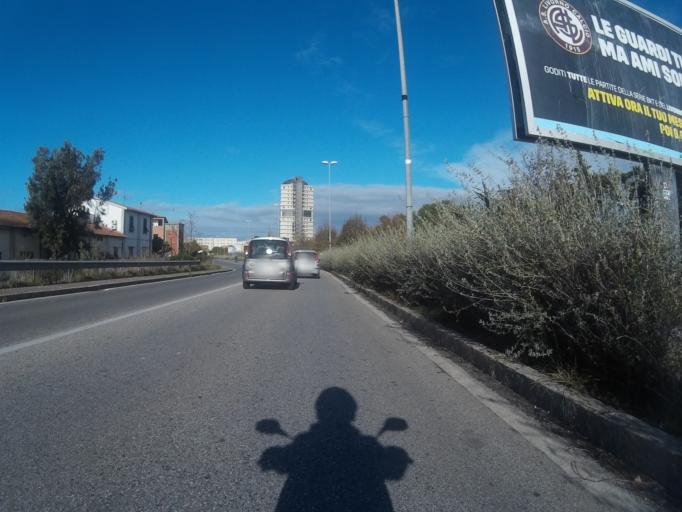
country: IT
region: Tuscany
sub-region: Provincia di Livorno
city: Livorno
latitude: 43.5583
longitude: 10.3421
